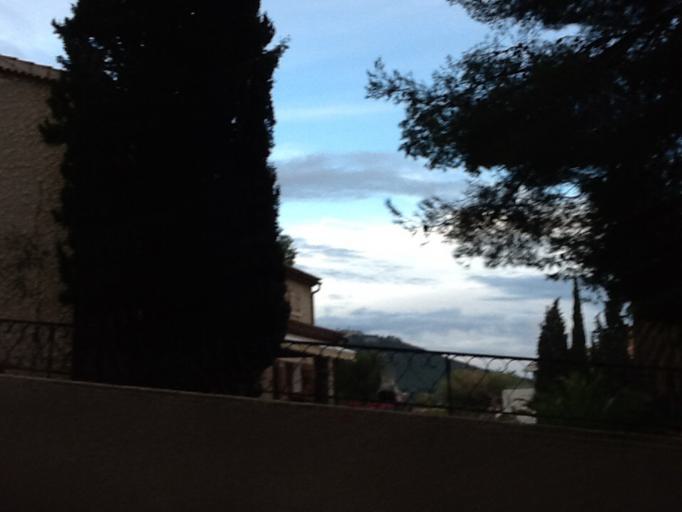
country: FR
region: Provence-Alpes-Cote d'Azur
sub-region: Departement du Var
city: Sanary-sur-Mer
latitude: 43.1094
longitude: 5.8177
